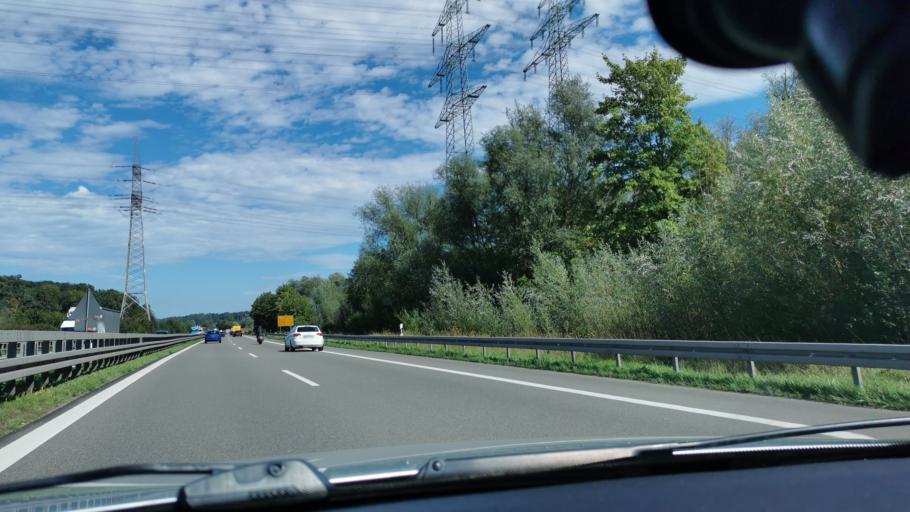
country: DE
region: Baden-Wuerttemberg
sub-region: Regierungsbezirk Stuttgart
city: Kongen
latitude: 48.6892
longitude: 9.3844
